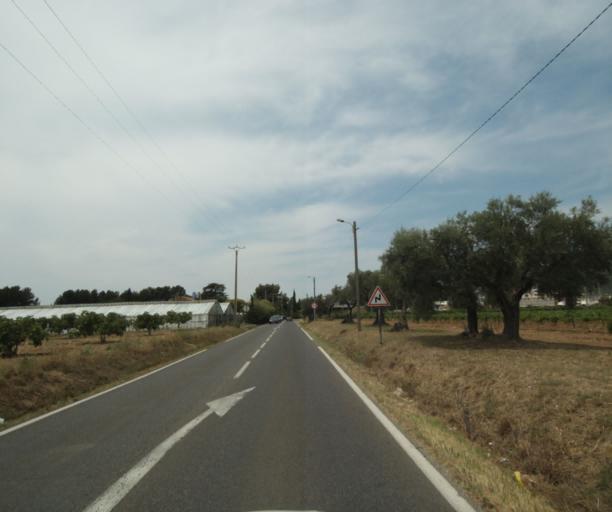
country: FR
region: Provence-Alpes-Cote d'Azur
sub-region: Departement du Var
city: La Farlede
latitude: 43.1402
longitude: 6.0415
